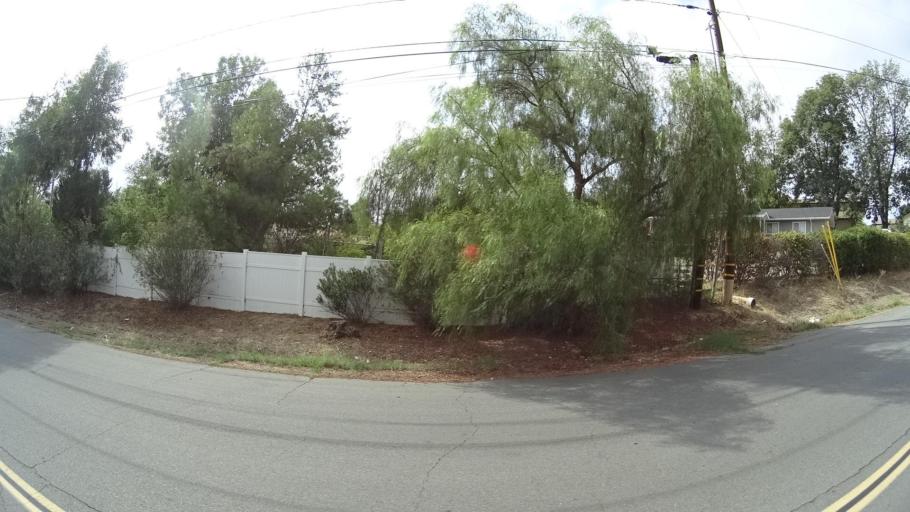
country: US
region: California
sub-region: San Diego County
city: Ramona
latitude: 33.0354
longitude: -116.8579
